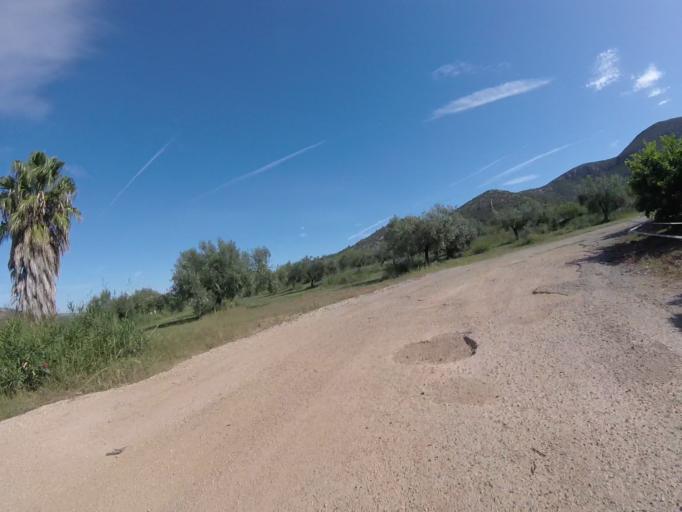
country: ES
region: Valencia
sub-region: Provincia de Castello
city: Santa Magdalena de Pulpis
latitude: 40.3804
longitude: 0.3366
